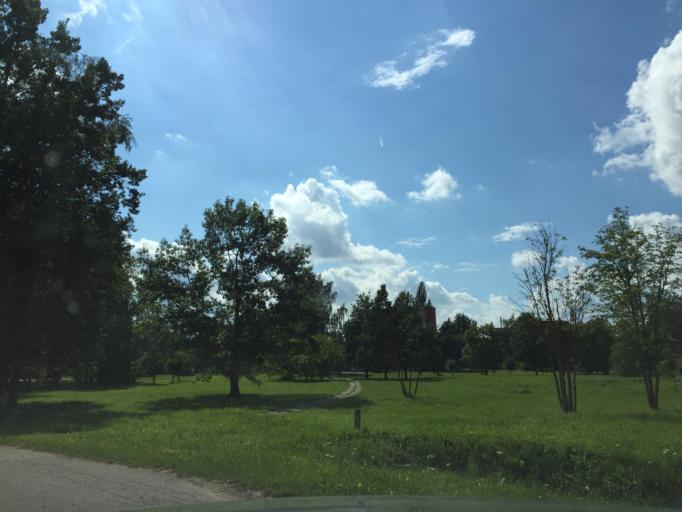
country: LV
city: Tervete
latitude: 56.6206
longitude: 23.4433
